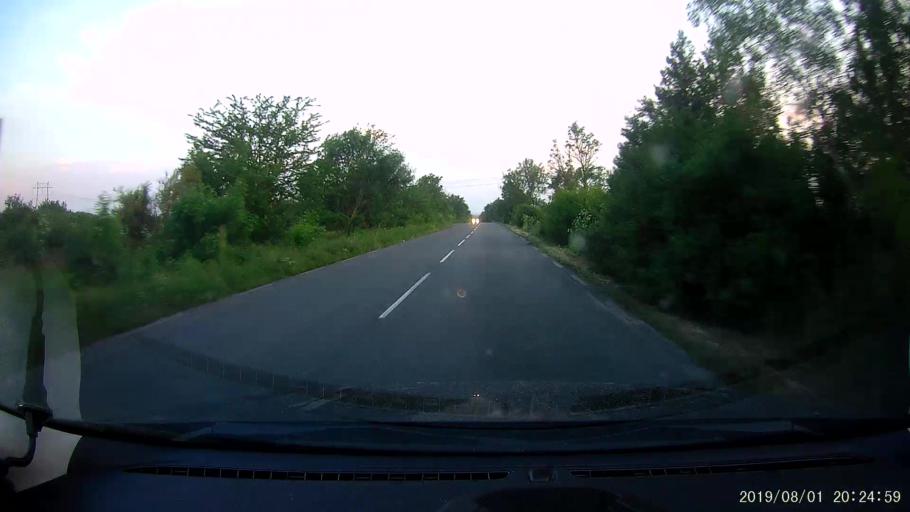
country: BG
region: Yambol
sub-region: Obshtina Elkhovo
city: Elkhovo
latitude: 42.2228
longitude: 26.5901
